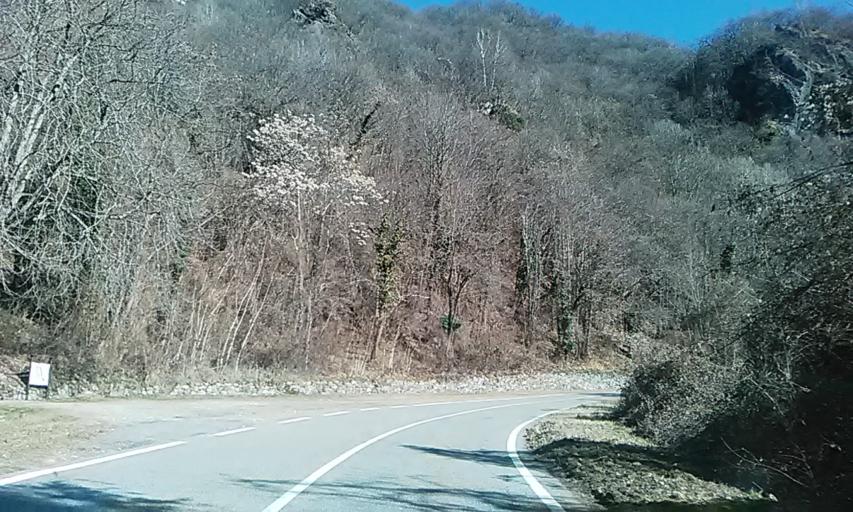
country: IT
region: Piedmont
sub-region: Provincia di Vercelli
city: Civiasco
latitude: 45.8036
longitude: 8.2814
